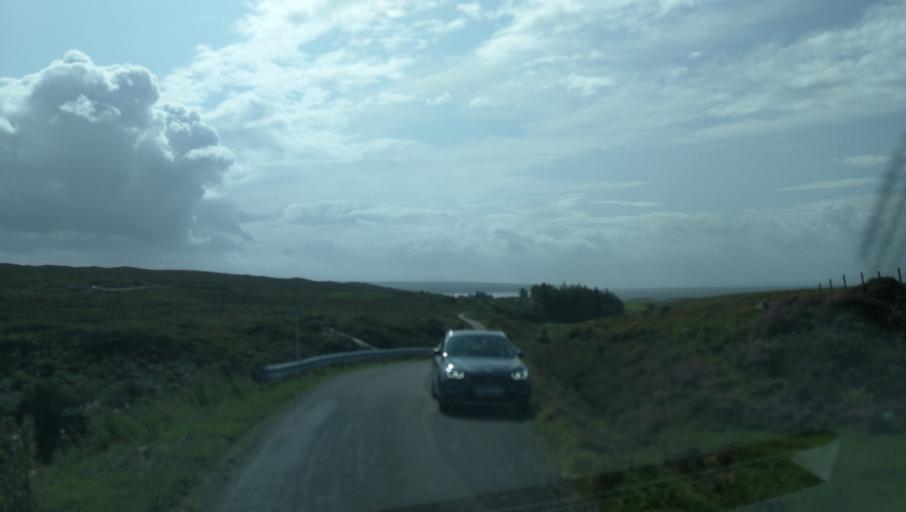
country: GB
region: Scotland
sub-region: Highland
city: Portree
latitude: 57.7491
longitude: -5.7620
